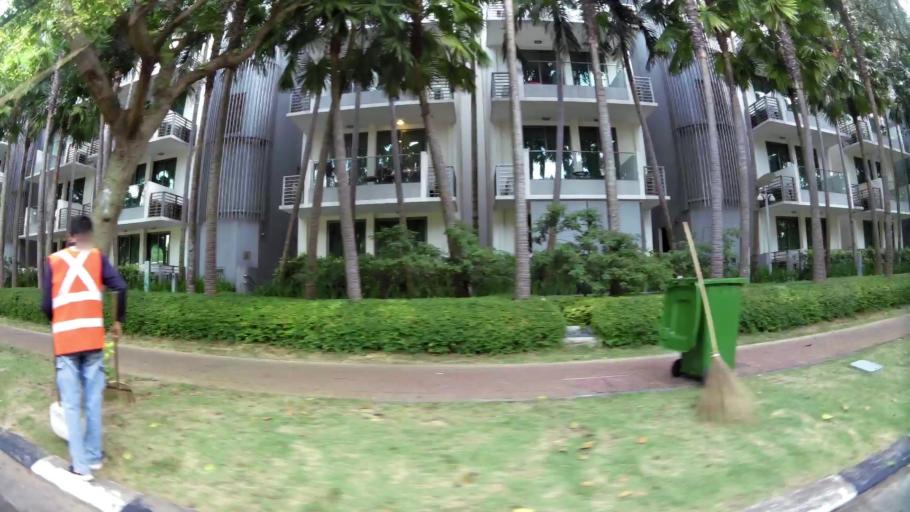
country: SG
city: Singapore
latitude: 1.2483
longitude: 103.8419
